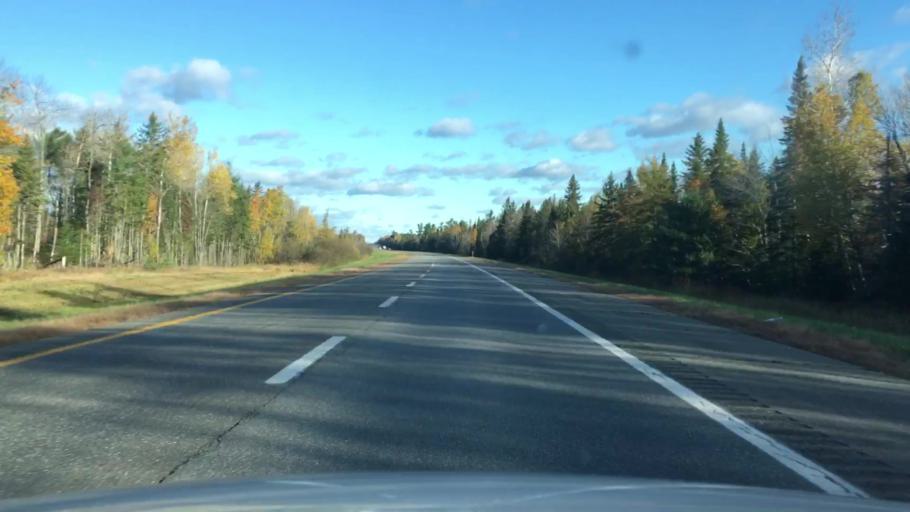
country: US
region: Maine
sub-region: Penobscot County
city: Greenbush
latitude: 45.0532
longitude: -68.6873
